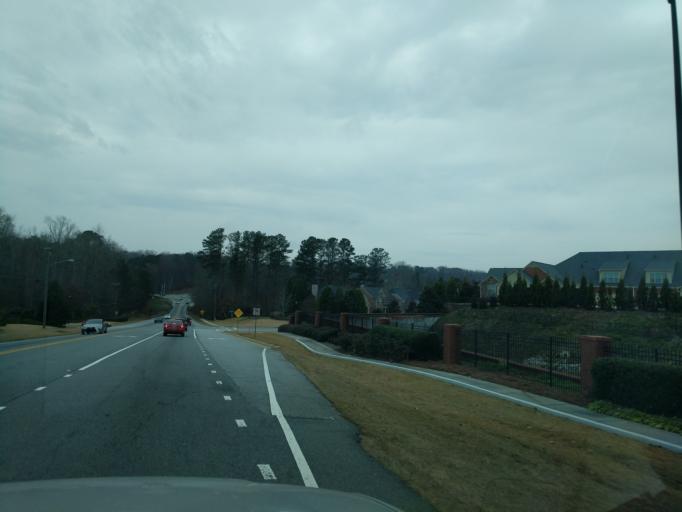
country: US
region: Georgia
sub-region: Gwinnett County
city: Duluth
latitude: 33.9786
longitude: -84.1058
